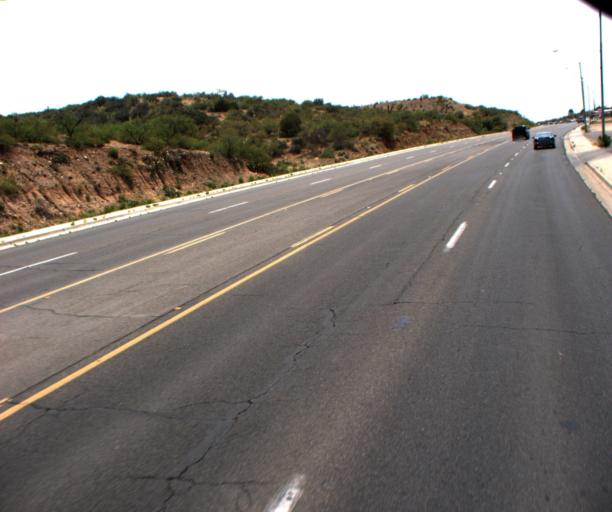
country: US
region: Arizona
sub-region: Gila County
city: Globe
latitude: 33.3906
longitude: -110.7632
